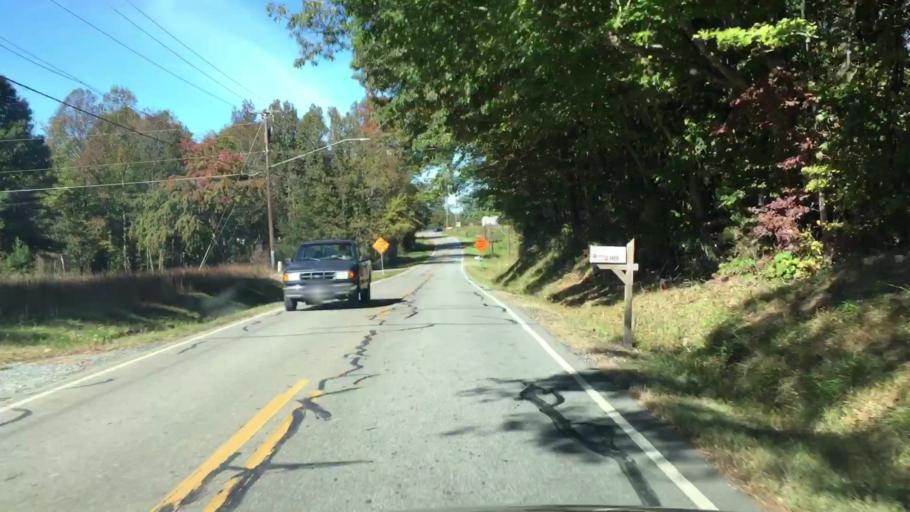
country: US
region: North Carolina
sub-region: Rockingham County
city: Reidsville
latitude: 36.3247
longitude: -79.6337
